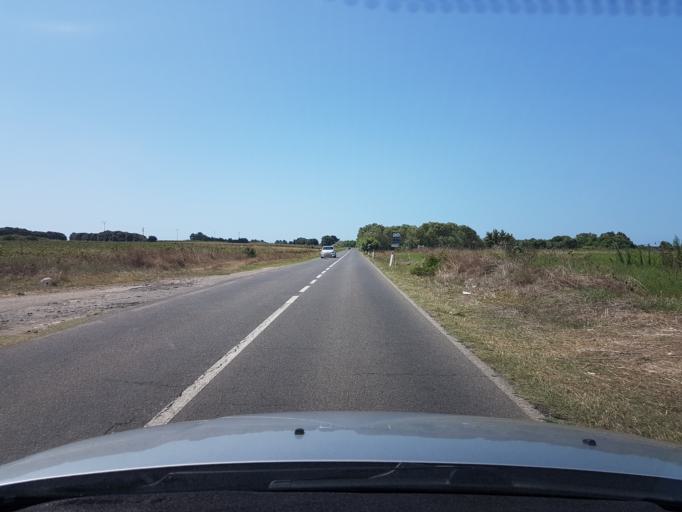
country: IT
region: Sardinia
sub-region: Provincia di Oristano
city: Riola Sardo
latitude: 40.0210
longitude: 8.4826
